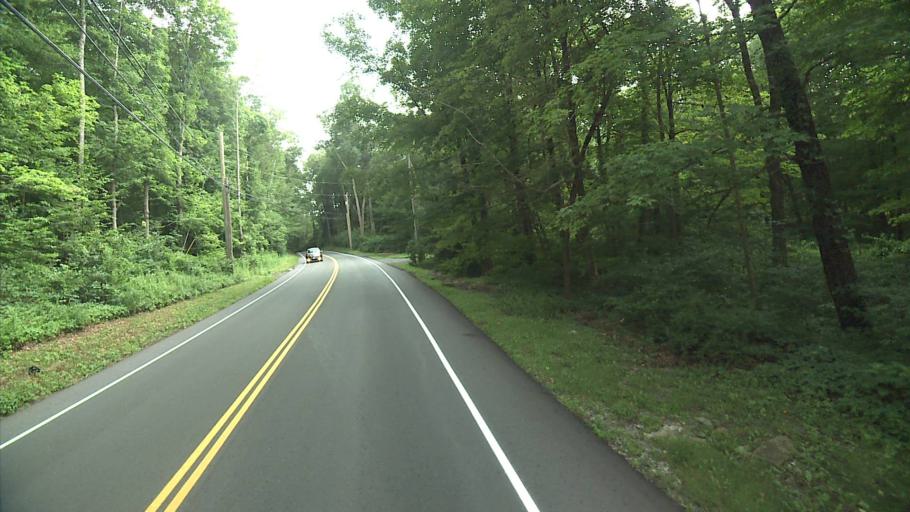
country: US
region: Connecticut
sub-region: New Haven County
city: Heritage Village
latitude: 41.5309
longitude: -73.2752
